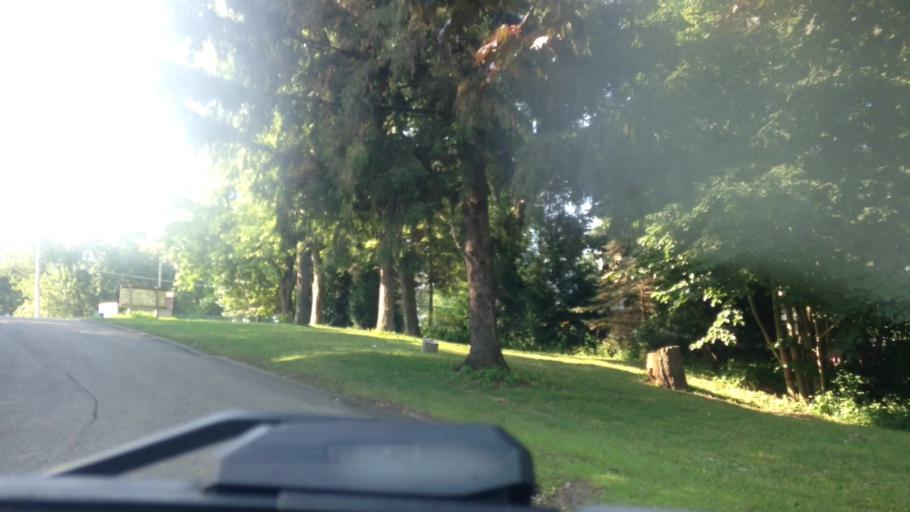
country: US
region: Wisconsin
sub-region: Waukesha County
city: Merton
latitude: 43.1632
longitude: -88.3104
